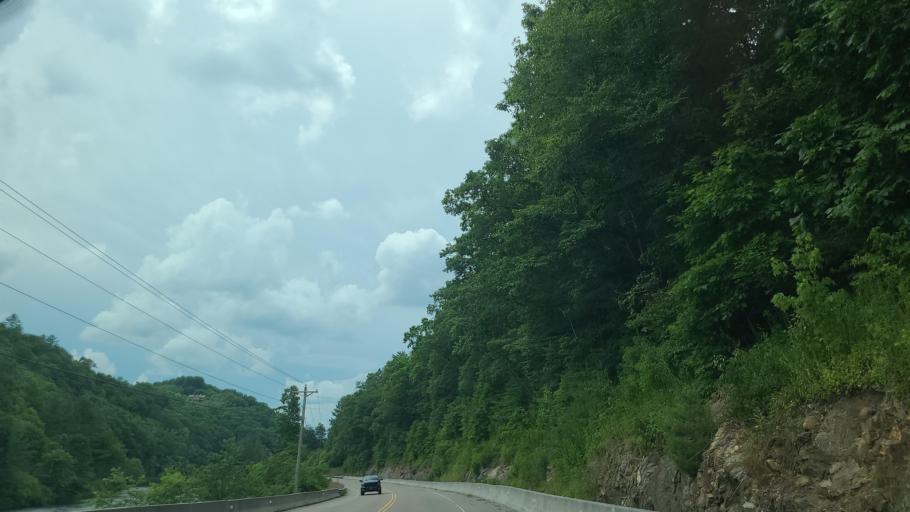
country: US
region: North Carolina
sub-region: Ashe County
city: Jefferson
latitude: 36.3765
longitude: -81.3980
